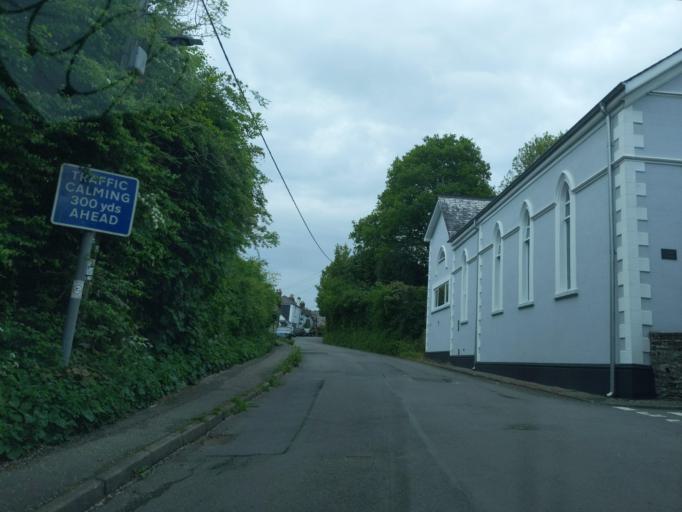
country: GB
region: England
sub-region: Devon
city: Horrabridge
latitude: 50.5119
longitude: -4.1005
